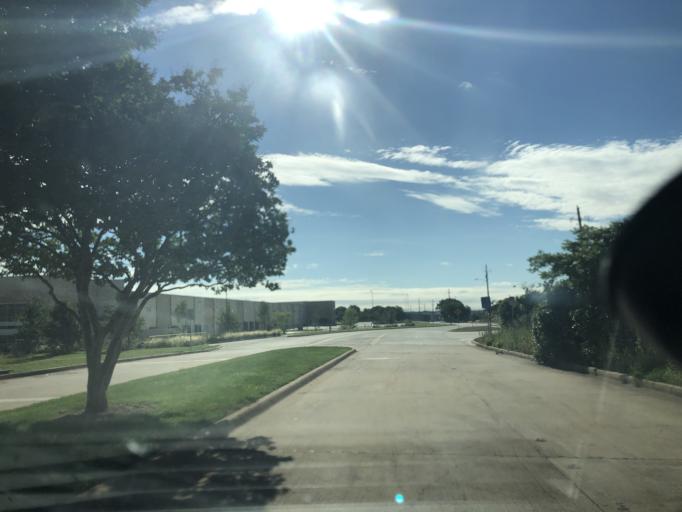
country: US
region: Texas
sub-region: Tarrant County
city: Euless
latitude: 32.8223
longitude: -97.0346
